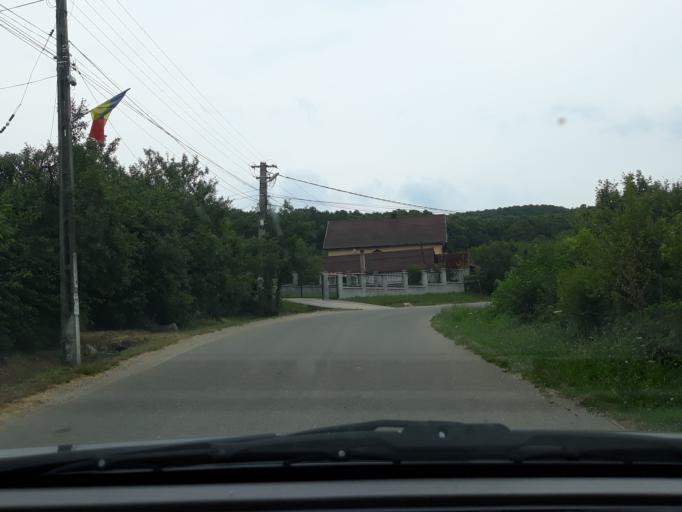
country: RO
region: Salaj
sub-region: Comuna Criseni
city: Criseni
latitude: 47.2508
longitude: 23.0709
